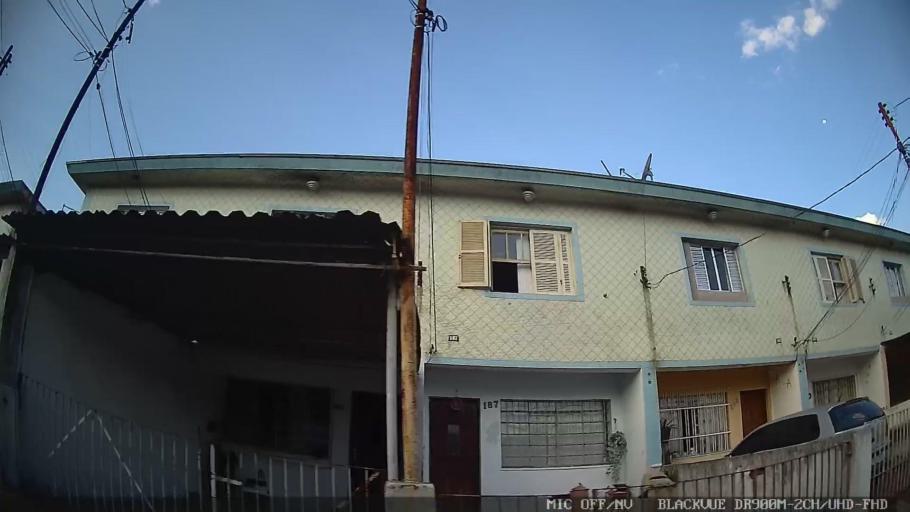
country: BR
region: Sao Paulo
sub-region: Sao Caetano Do Sul
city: Sao Caetano do Sul
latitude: -23.5783
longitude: -46.5556
